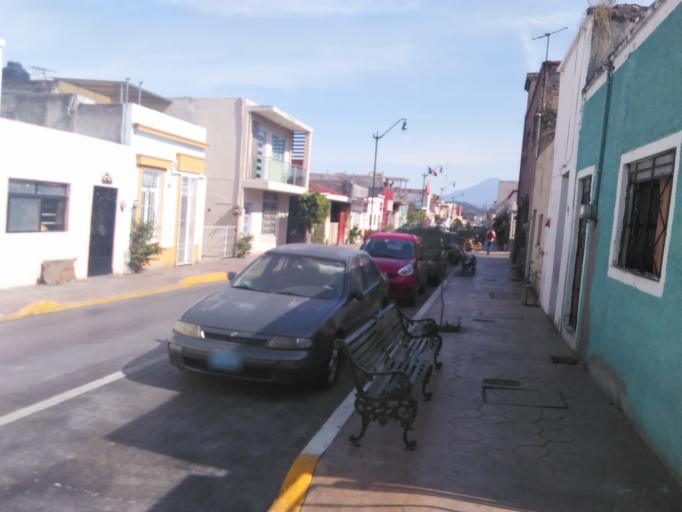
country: MX
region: Nayarit
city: Tepic
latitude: 21.5133
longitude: -104.8983
